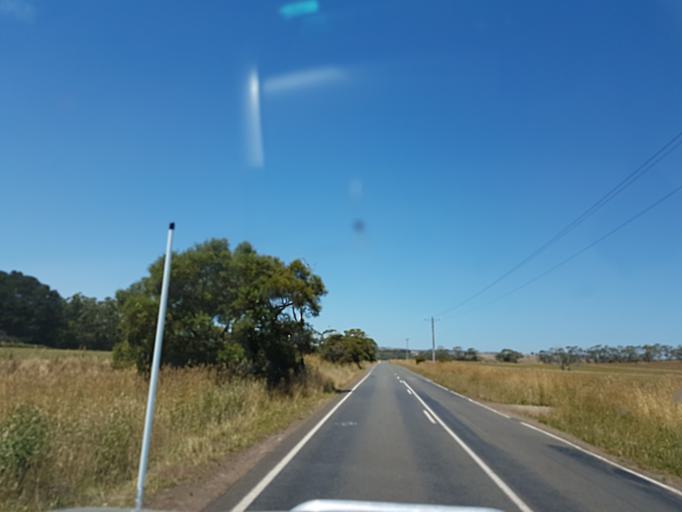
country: AU
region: Victoria
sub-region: Warrnambool
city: Allansford
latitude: -38.4536
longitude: 143.0478
